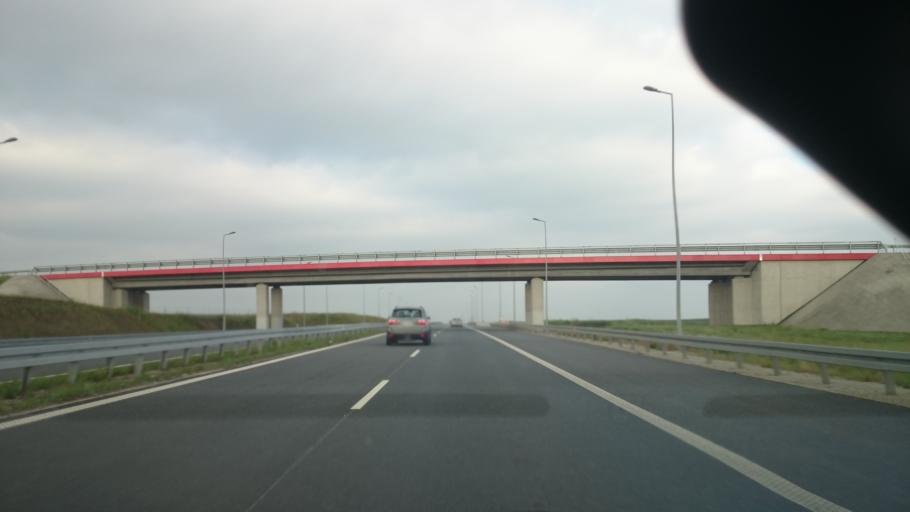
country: PL
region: Opole Voivodeship
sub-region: Powiat nyski
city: Nysa
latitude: 50.5014
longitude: 17.3307
